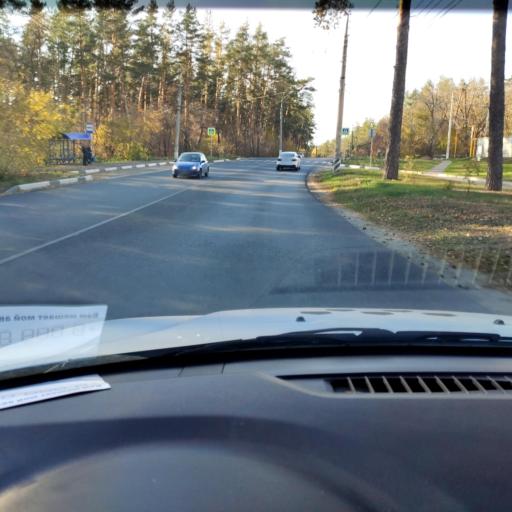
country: RU
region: Samara
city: Tol'yatti
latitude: 53.4781
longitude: 49.3592
